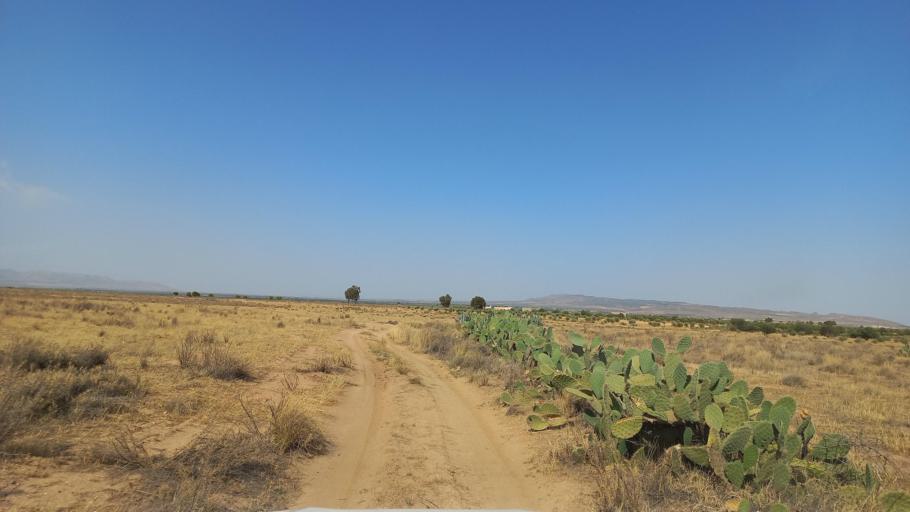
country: TN
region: Al Qasrayn
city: Kasserine
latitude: 35.2141
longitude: 9.0317
